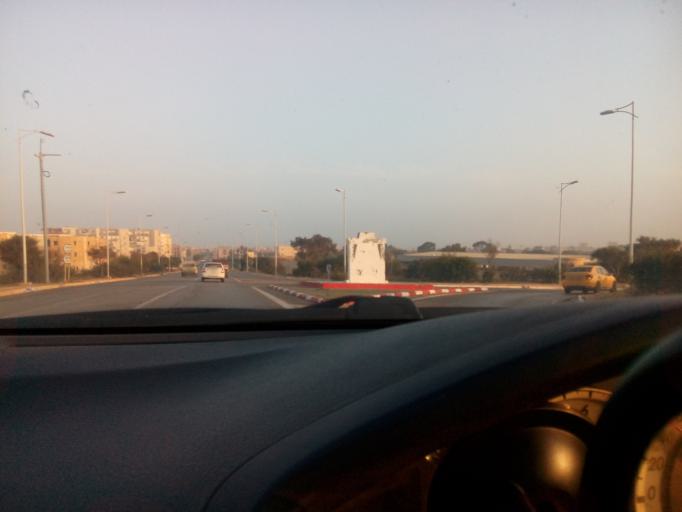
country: DZ
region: Oran
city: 'Ain el Turk
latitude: 35.7314
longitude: -0.7723
